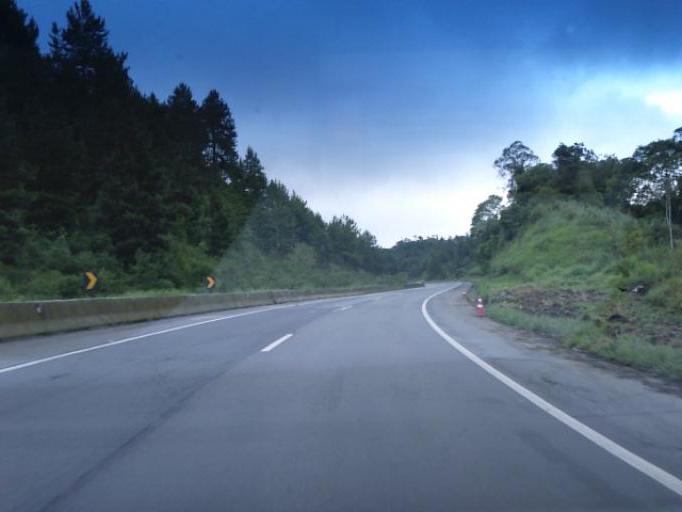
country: BR
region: Parana
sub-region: Antonina
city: Antonina
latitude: -25.0555
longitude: -48.5544
